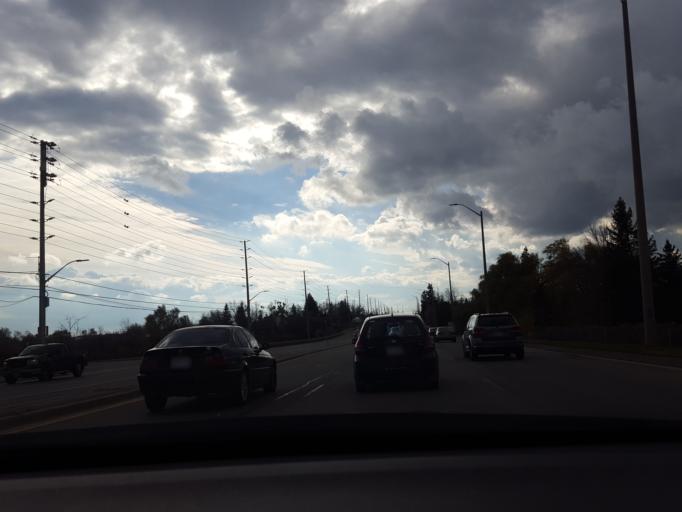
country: CA
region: Ontario
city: Brampton
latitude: 43.6436
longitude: -79.7092
